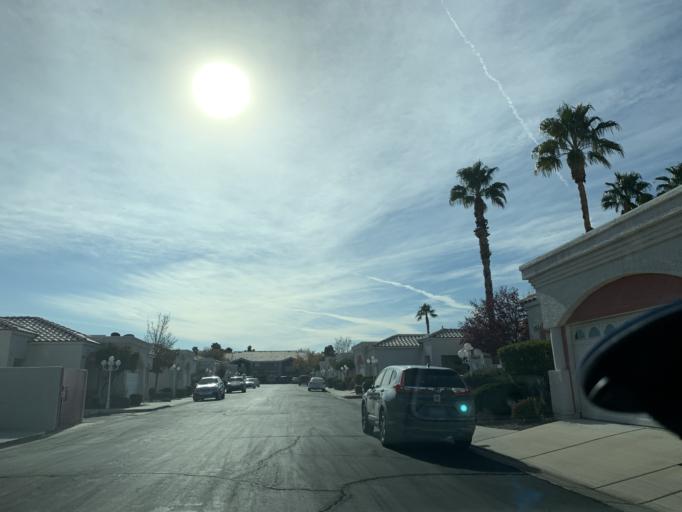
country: US
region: Nevada
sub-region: Clark County
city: Spring Valley
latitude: 36.0963
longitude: -115.2141
